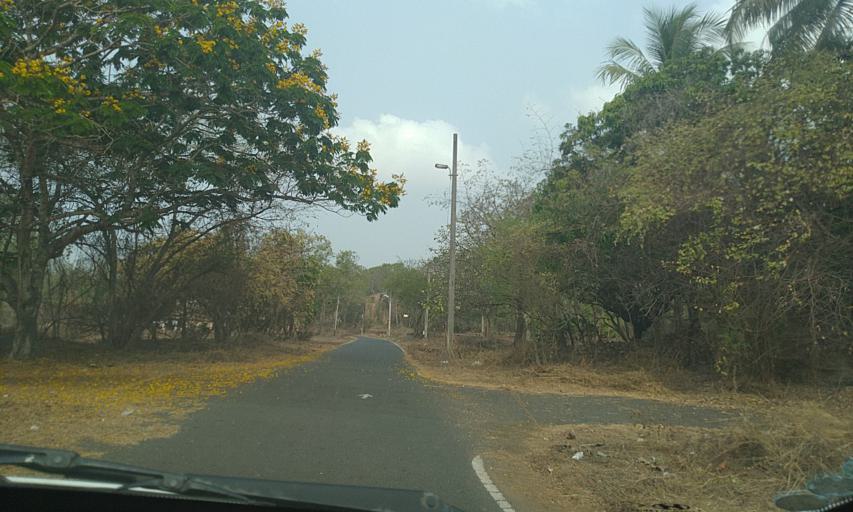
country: IN
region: Goa
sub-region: North Goa
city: Taleigao
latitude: 15.4548
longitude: 73.8381
